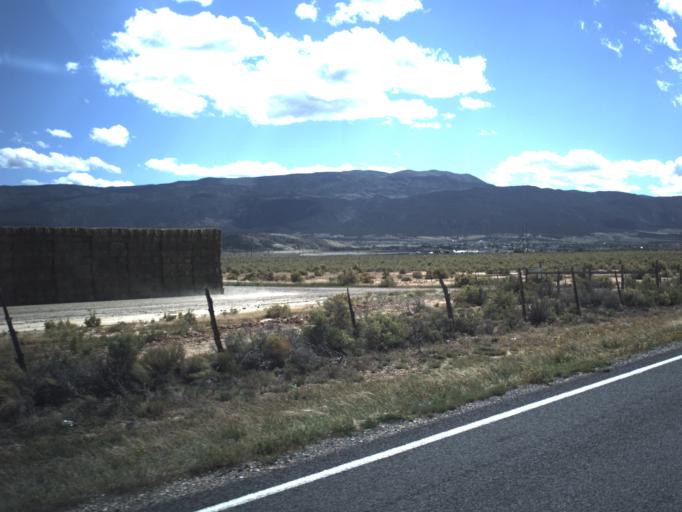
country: US
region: Utah
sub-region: Iron County
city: Enoch
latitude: 37.8102
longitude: -113.0505
